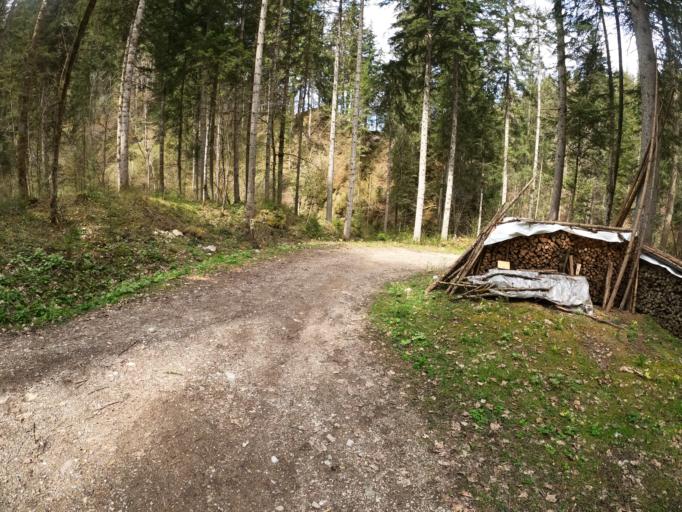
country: AT
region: Salzburg
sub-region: Politischer Bezirk Sankt Johann im Pongau
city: Pfarrwerfen
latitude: 47.4586
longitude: 13.2261
